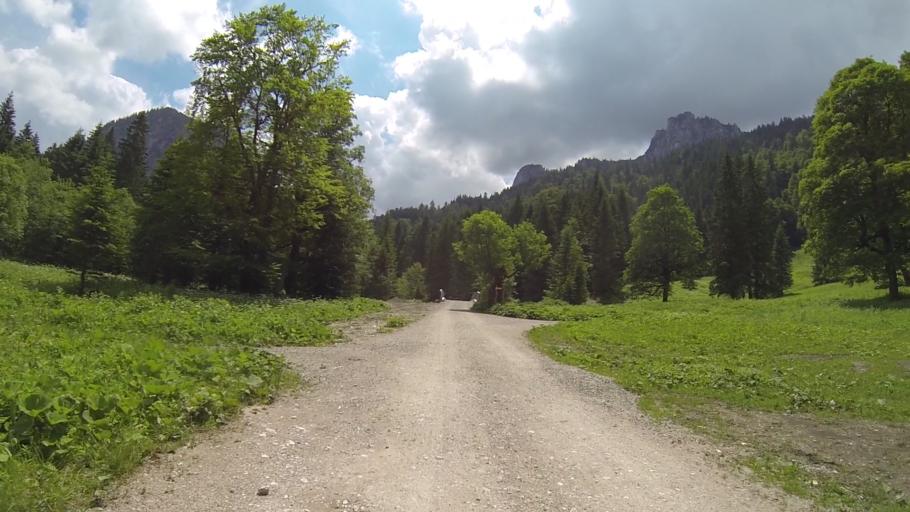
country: DE
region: Bavaria
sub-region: Swabia
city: Schwangau
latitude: 47.5382
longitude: 10.7750
